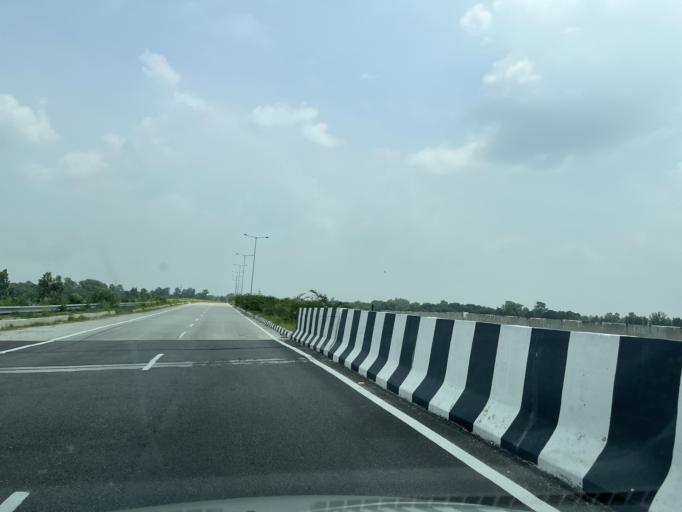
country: IN
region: Uttar Pradesh
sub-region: Bijnor
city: Nagina
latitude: 29.4250
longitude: 78.4307
